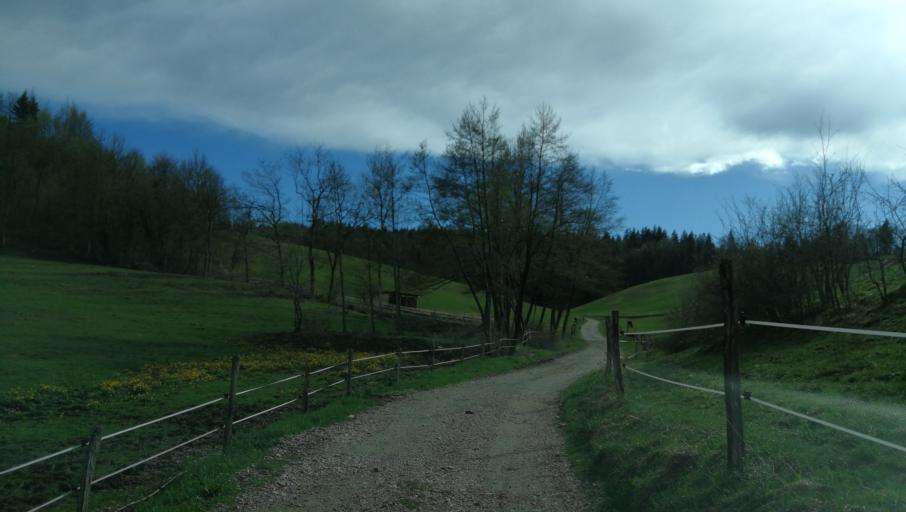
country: FR
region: Franche-Comte
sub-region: Departement du Jura
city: Lavans-les-Saint-Claude
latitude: 46.3085
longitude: 5.8086
